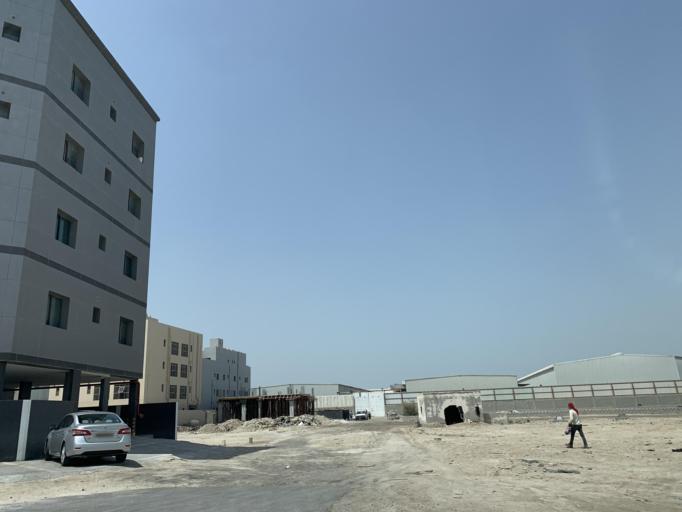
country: BH
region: Northern
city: Madinat `Isa
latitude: 26.1909
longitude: 50.5470
